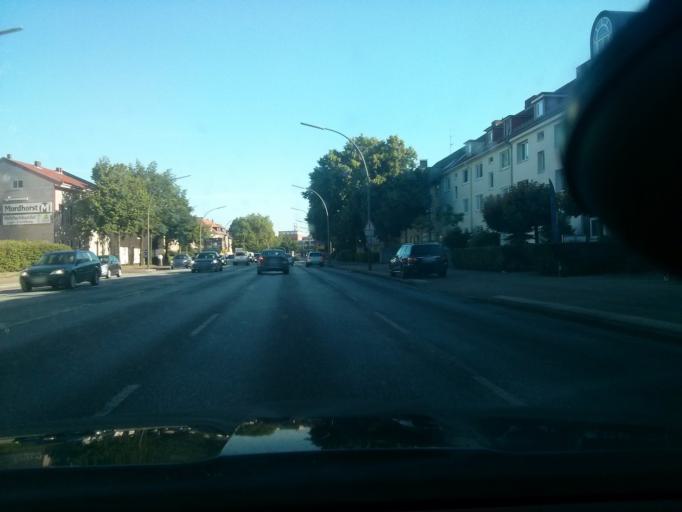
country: DE
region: Hamburg
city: Stellingen
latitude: 53.5885
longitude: 9.9315
